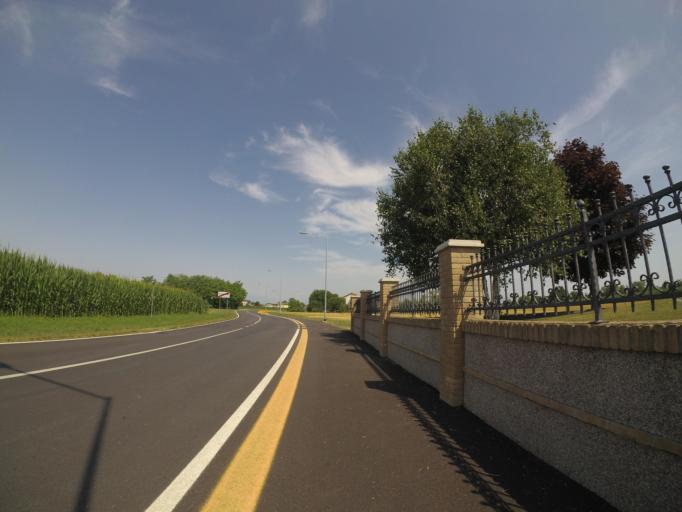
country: IT
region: Friuli Venezia Giulia
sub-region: Provincia di Pordenone
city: Rosa
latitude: 45.9203
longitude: 12.8757
